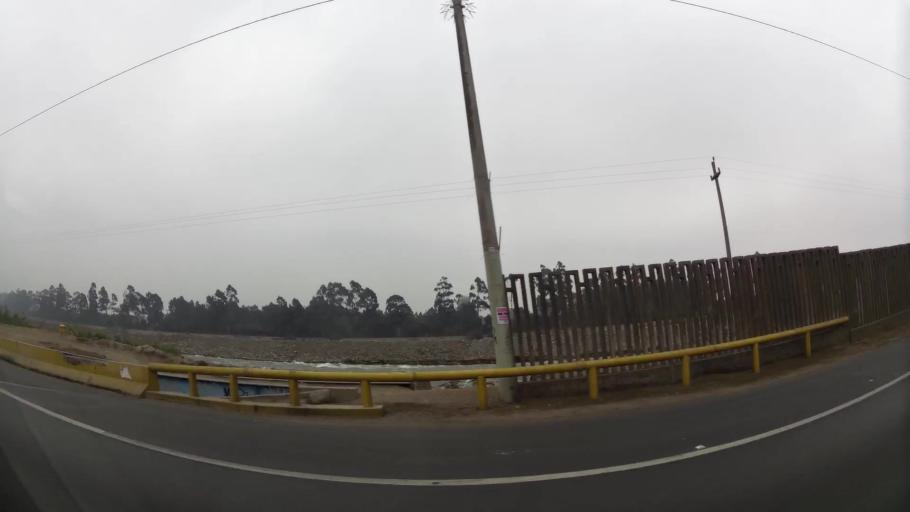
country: PE
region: Lima
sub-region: Lima
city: Vitarte
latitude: -12.0204
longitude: -76.9524
